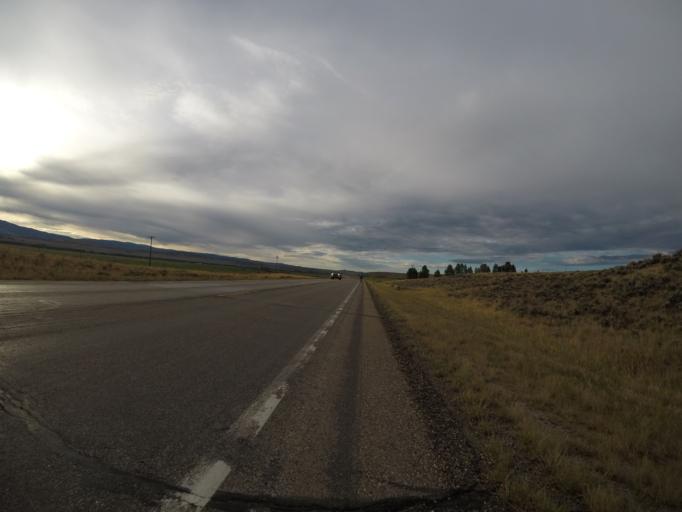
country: US
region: Wyoming
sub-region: Carbon County
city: Saratoga
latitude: 41.4002
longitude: -106.7696
